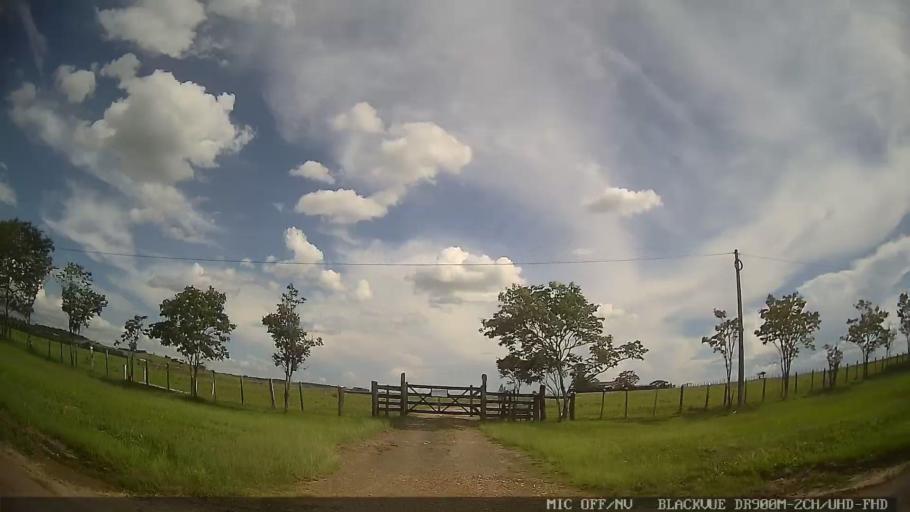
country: BR
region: Sao Paulo
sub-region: Conchas
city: Conchas
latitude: -23.0454
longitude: -47.9467
